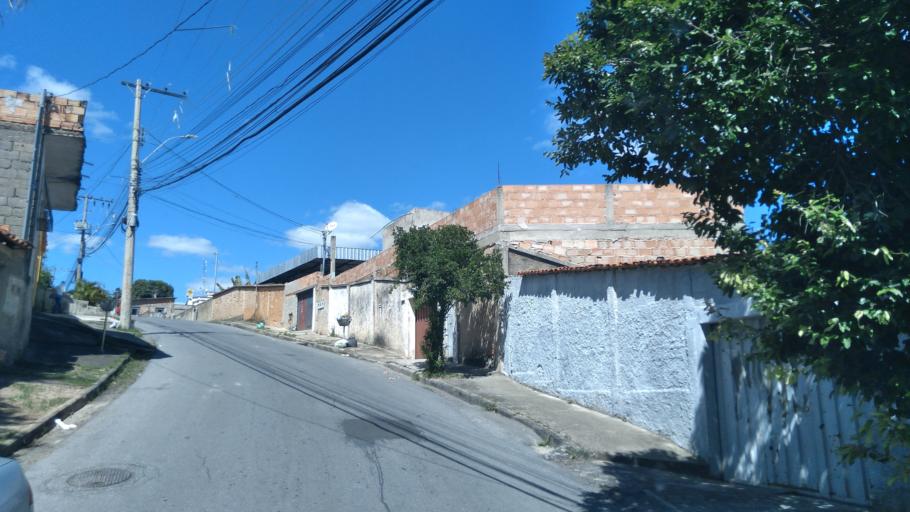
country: BR
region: Minas Gerais
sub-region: Belo Horizonte
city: Belo Horizonte
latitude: -19.8543
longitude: -43.8851
